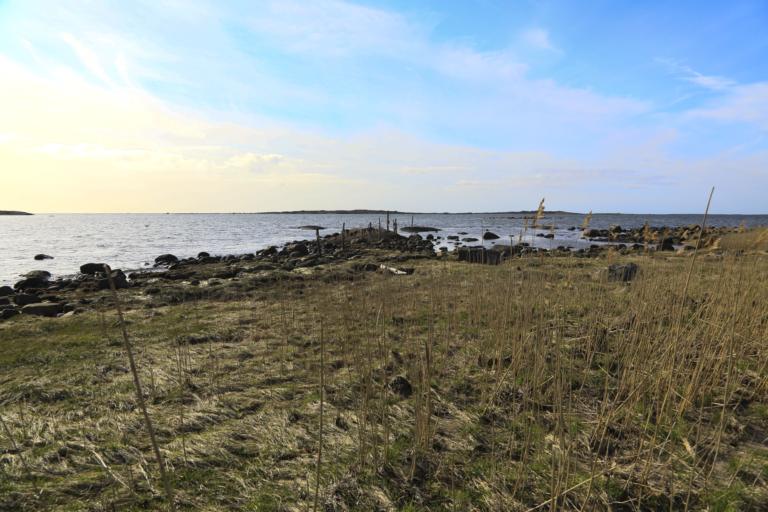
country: SE
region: Halland
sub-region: Varbergs Kommun
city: Varberg
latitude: 57.1246
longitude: 12.2032
